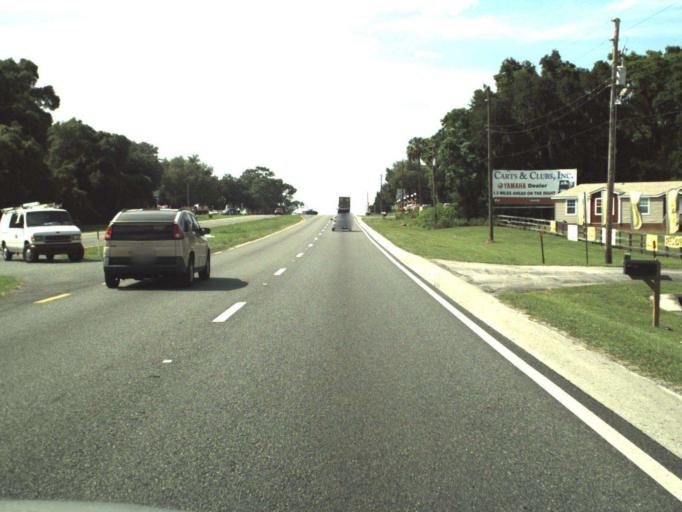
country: US
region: Florida
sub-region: Marion County
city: Ocala
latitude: 29.1260
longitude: -82.1025
